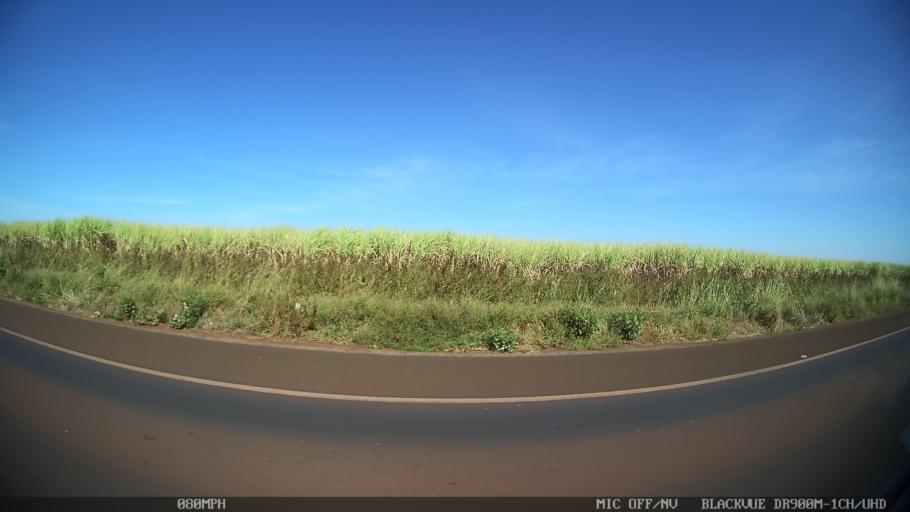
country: BR
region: Sao Paulo
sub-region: Guaira
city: Guaira
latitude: -20.4441
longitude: -48.3578
